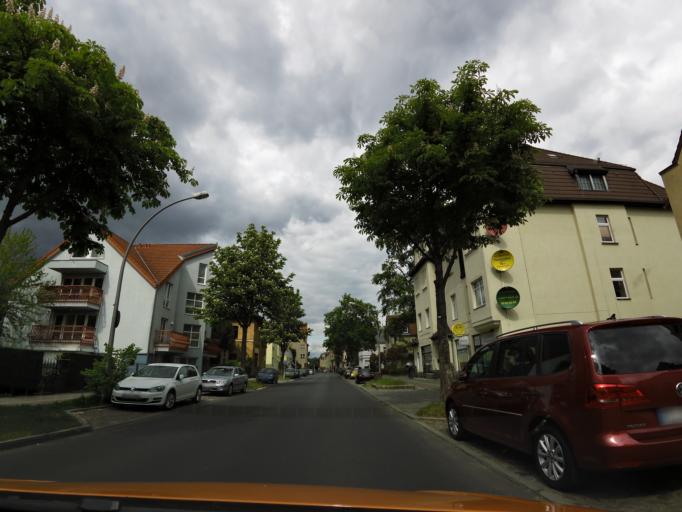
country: DE
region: Berlin
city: Zehlendorf Bezirk
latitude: 52.4279
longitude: 13.2552
